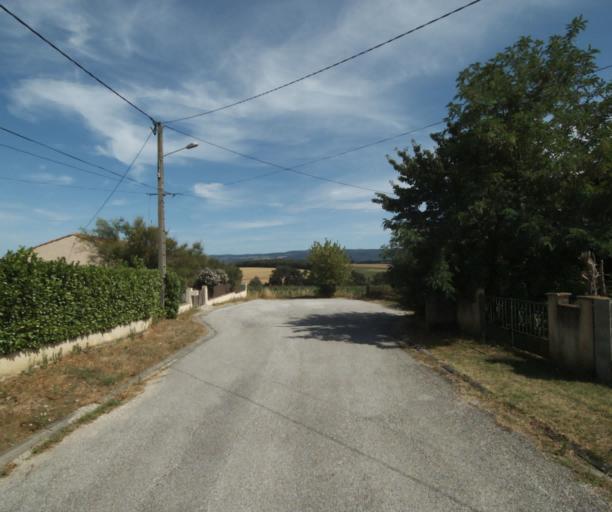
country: FR
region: Midi-Pyrenees
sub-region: Departement de la Haute-Garonne
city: Revel
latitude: 43.5093
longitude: 2.0354
